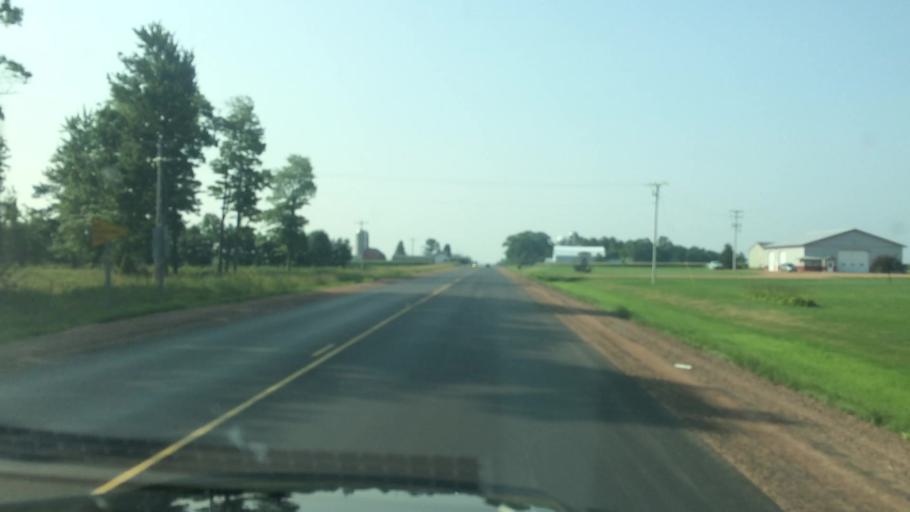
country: US
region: Wisconsin
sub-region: Marathon County
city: Stratford
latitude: 44.8567
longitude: -90.0792
